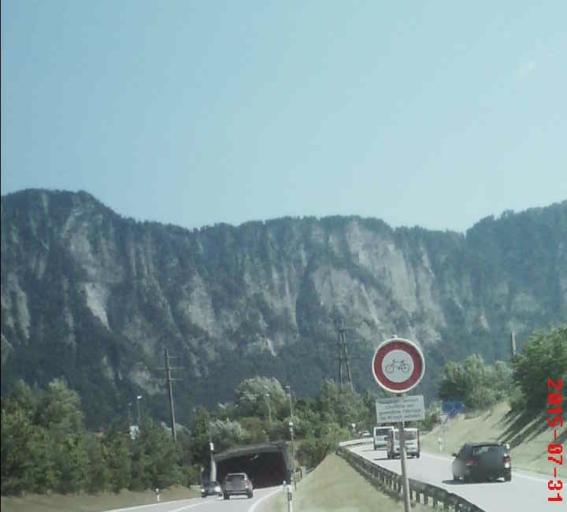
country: CH
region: Grisons
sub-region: Landquart District
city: Malans
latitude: 46.9706
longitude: 9.5586
